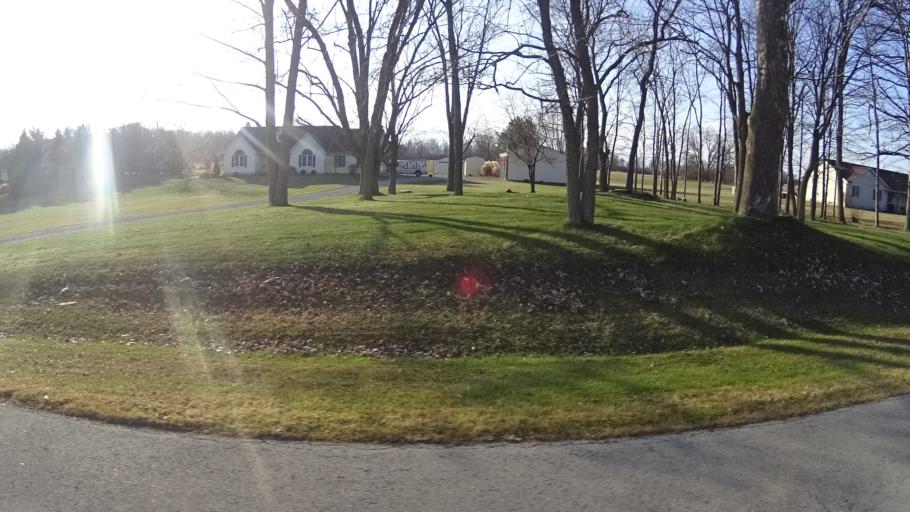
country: US
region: Ohio
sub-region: Lorain County
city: Oberlin
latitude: 41.2504
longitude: -82.2499
